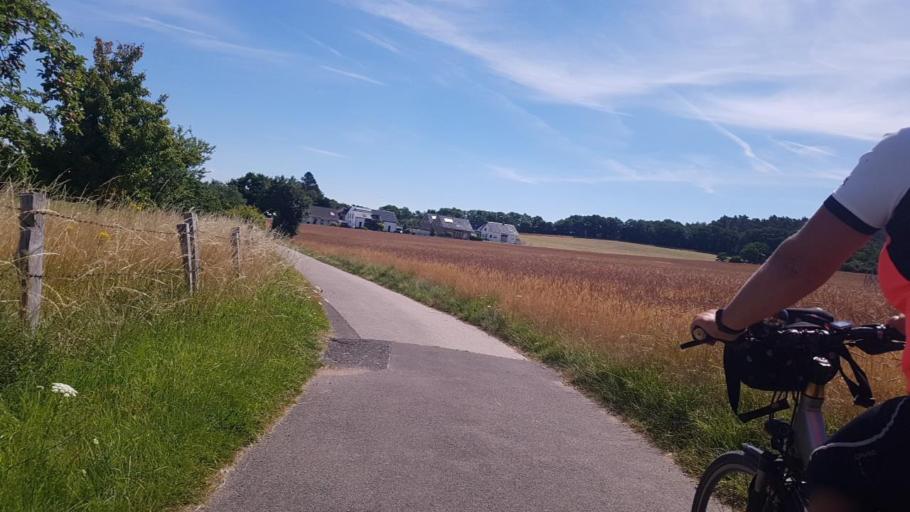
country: DE
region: North Rhine-Westphalia
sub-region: Regierungsbezirk Koln
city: Mechernich
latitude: 50.6266
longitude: 6.6794
